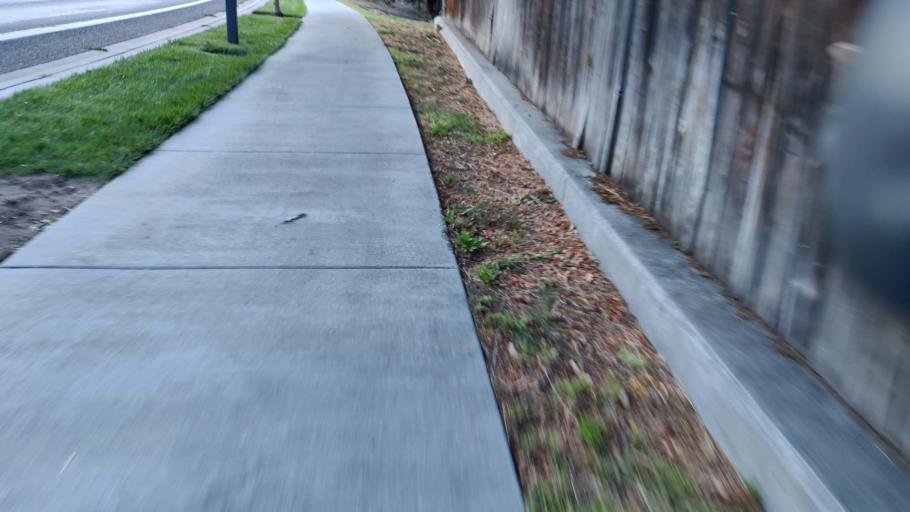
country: US
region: Idaho
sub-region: Ada County
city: Boise
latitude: 43.6068
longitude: -116.1902
